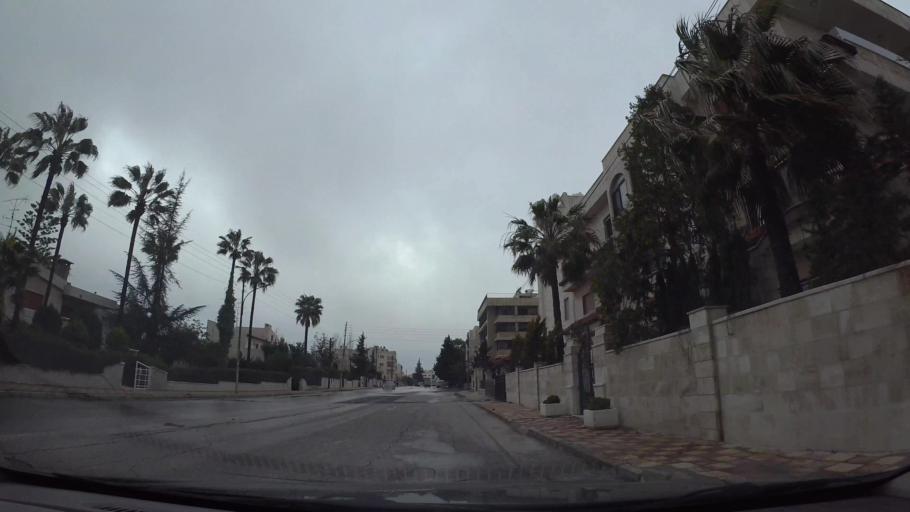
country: JO
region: Amman
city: Wadi as Sir
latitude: 31.9542
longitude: 35.8746
